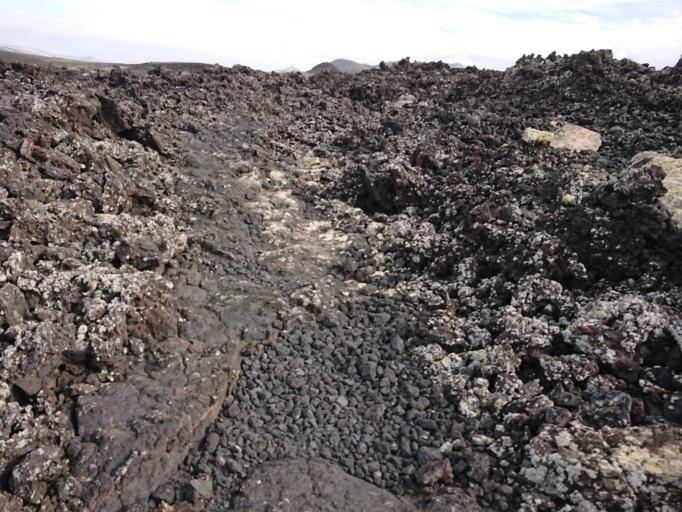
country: ES
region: Canary Islands
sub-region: Provincia de Las Palmas
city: Tinajo
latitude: 29.0114
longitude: -13.6771
